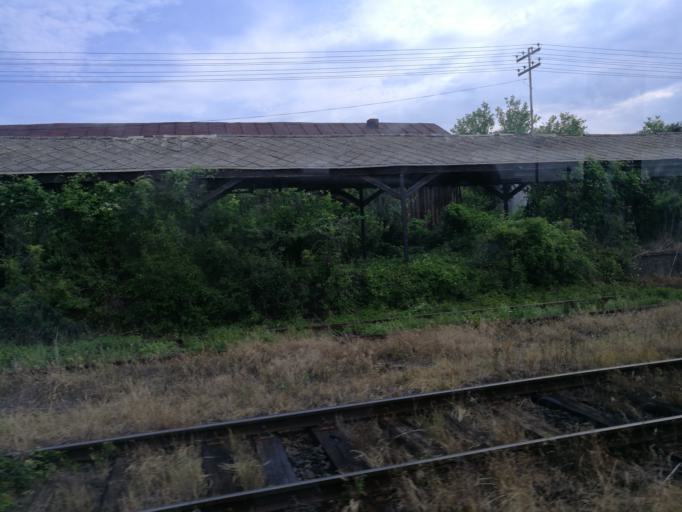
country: RO
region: Arges
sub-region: Oras Stefanesti
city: Golesti
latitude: 44.8368
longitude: 24.9643
